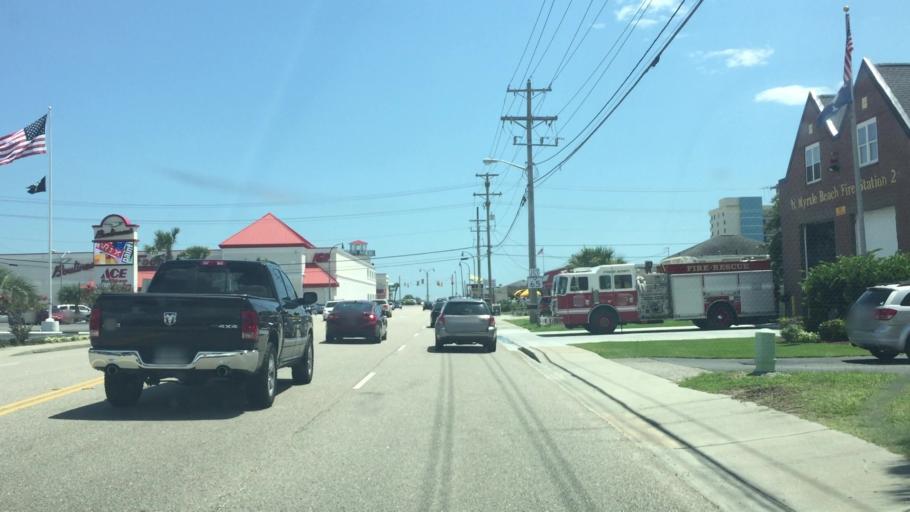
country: US
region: South Carolina
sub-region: Horry County
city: North Myrtle Beach
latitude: 33.8303
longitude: -78.6439
